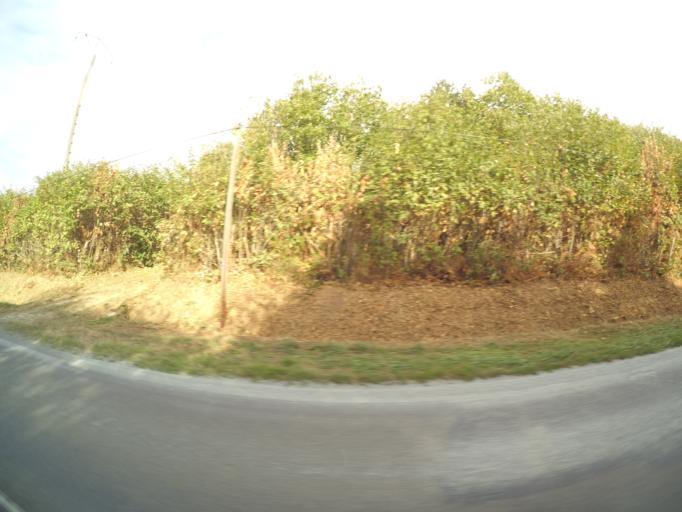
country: FR
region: Pays de la Loire
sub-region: Departement de Maine-et-Loire
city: Villedieu-la-Blouere
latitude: 47.1832
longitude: -1.0716
